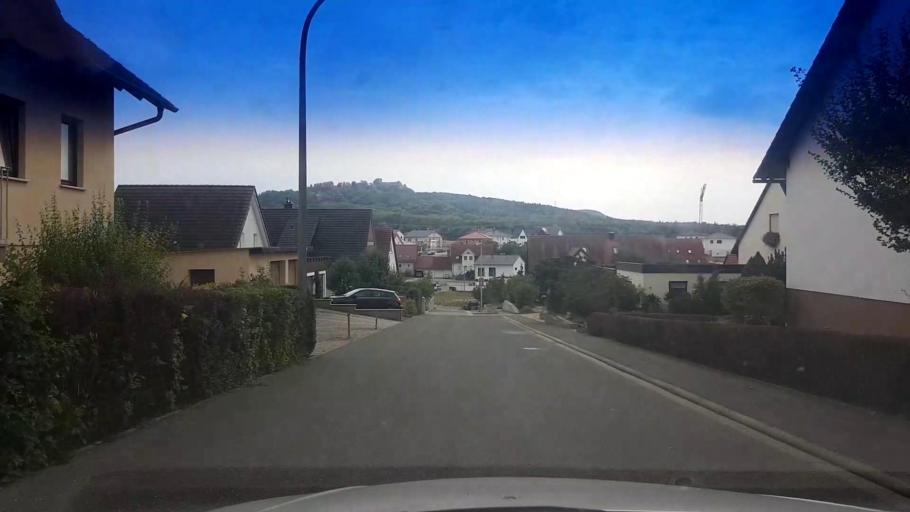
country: DE
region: Bavaria
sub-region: Upper Franconia
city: Schesslitz
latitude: 49.9754
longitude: 11.0474
